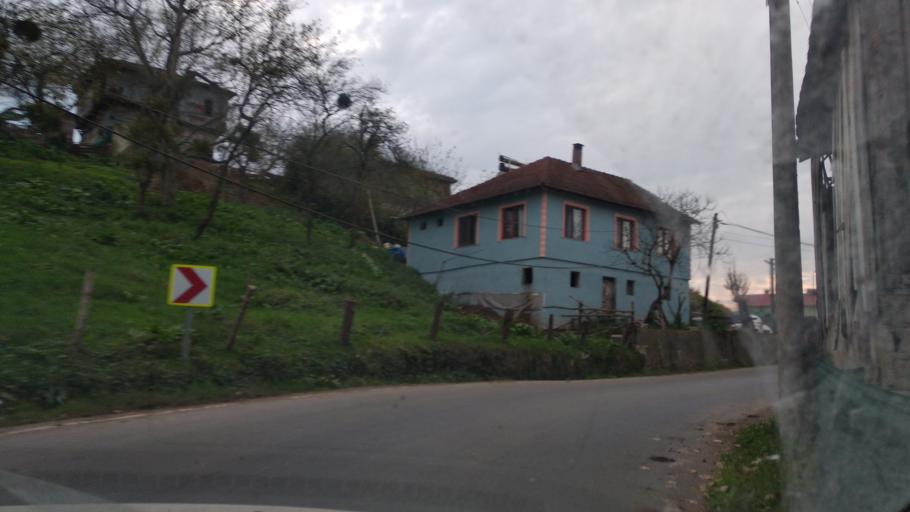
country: TR
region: Sakarya
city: Ortakoy
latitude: 41.0368
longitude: 30.6476
